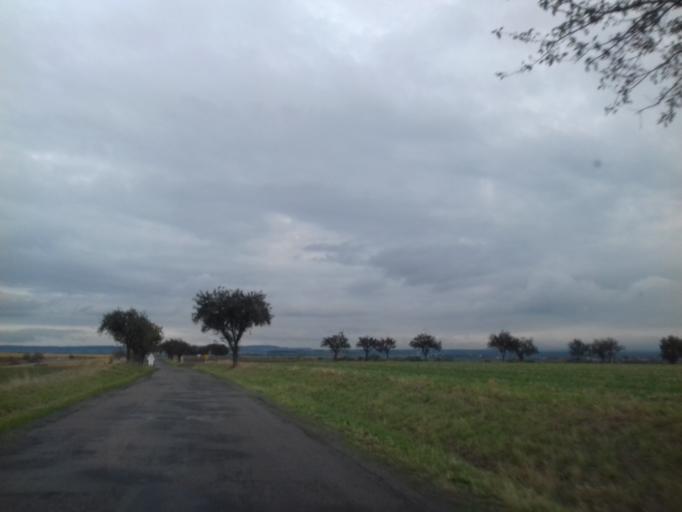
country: CZ
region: Pardubicky
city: Hrochuv Tynec
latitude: 49.9241
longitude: 15.8792
